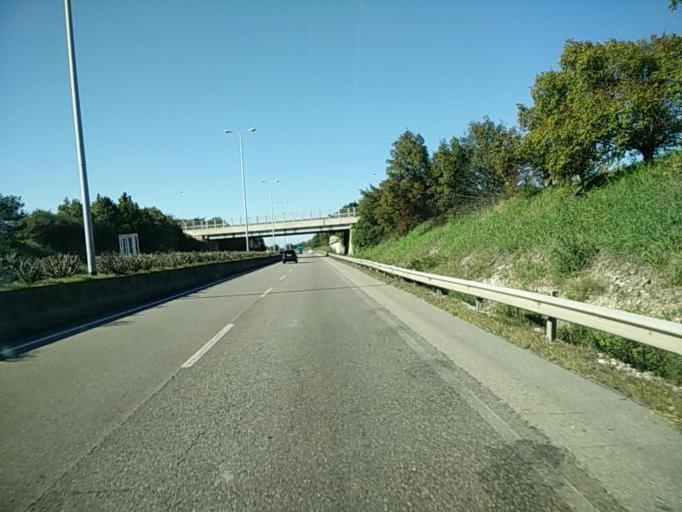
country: IT
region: Veneto
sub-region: Provincia di Verona
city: Caselle
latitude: 45.4304
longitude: 10.9294
